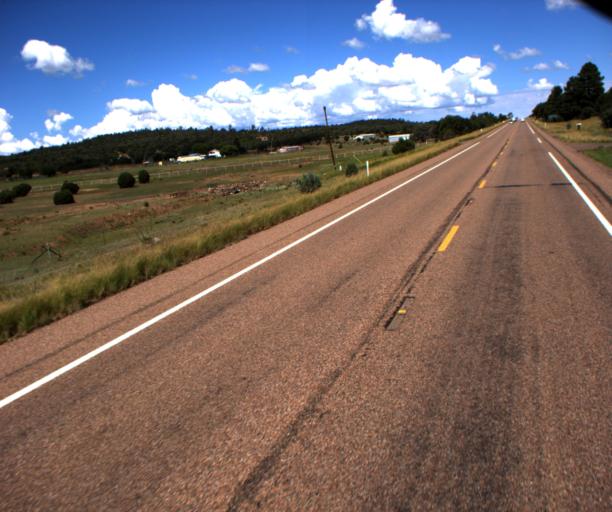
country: US
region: Arizona
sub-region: Navajo County
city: Linden
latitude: 34.3305
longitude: -110.2647
